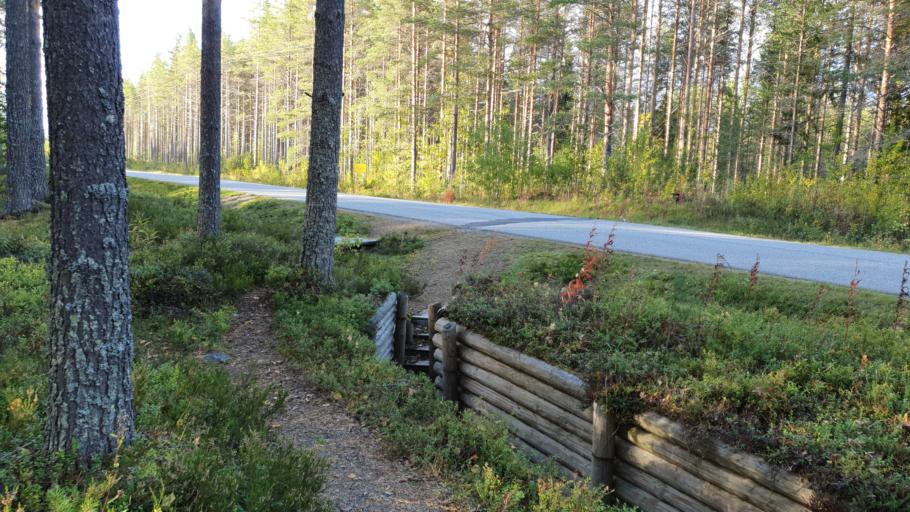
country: FI
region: Kainuu
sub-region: Kehys-Kainuu
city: Kuhmo
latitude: 63.9312
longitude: 29.9718
